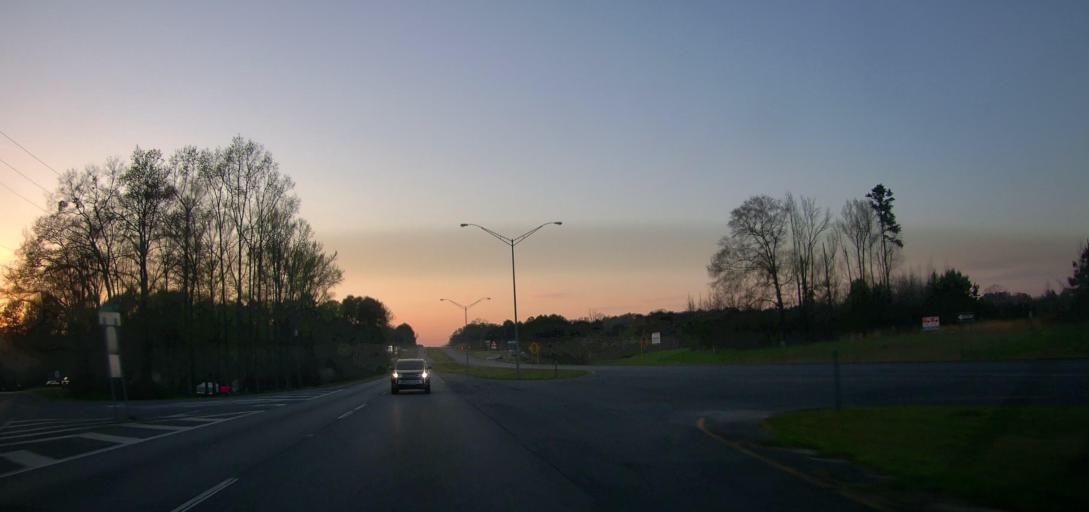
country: US
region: Alabama
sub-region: Tallapoosa County
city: Alexander City
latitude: 32.9366
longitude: -85.9751
